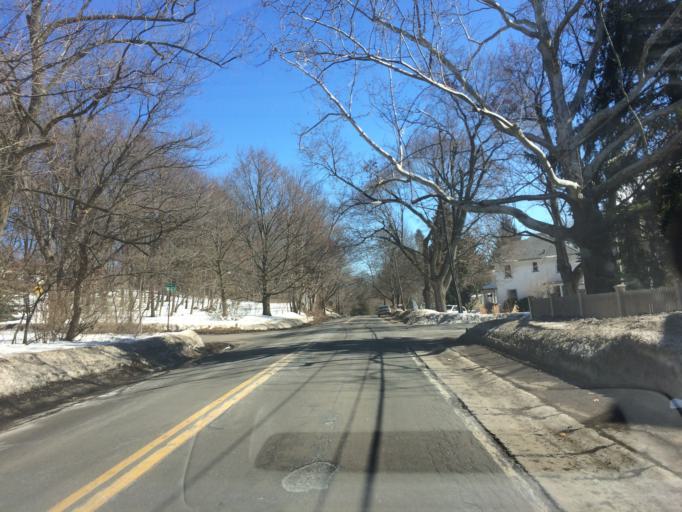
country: US
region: New York
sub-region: Monroe County
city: Rochester
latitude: 43.1307
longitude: -77.5960
